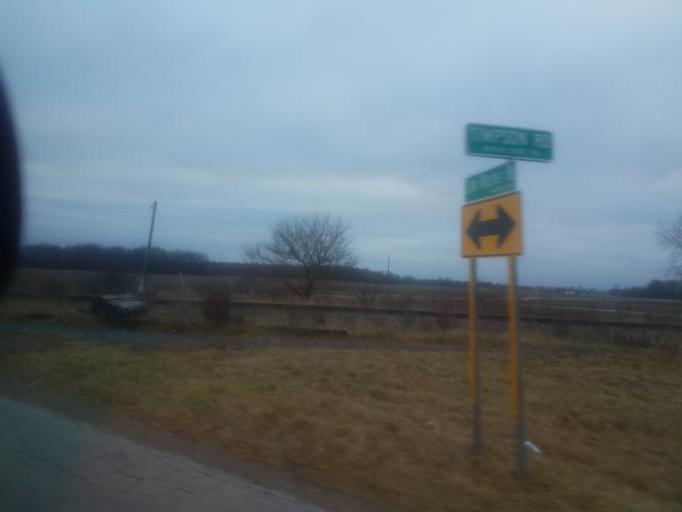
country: US
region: Ohio
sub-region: Morrow County
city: Mount Gilead
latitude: 40.6529
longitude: -82.9393
